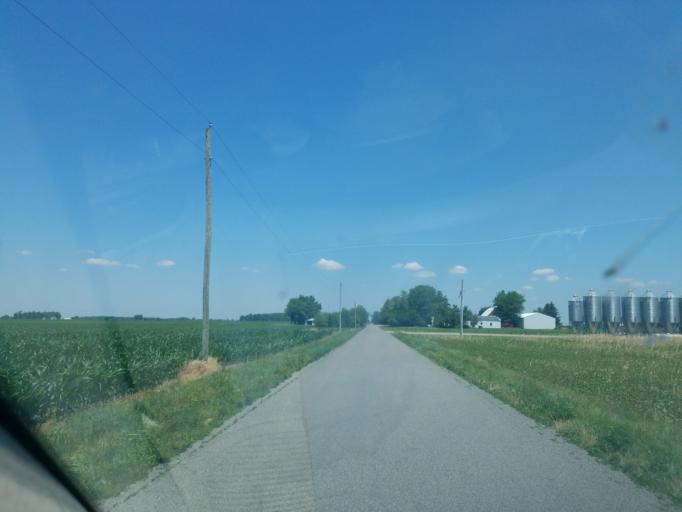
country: US
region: Ohio
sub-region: Allen County
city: Spencerville
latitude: 40.7614
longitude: -84.3494
